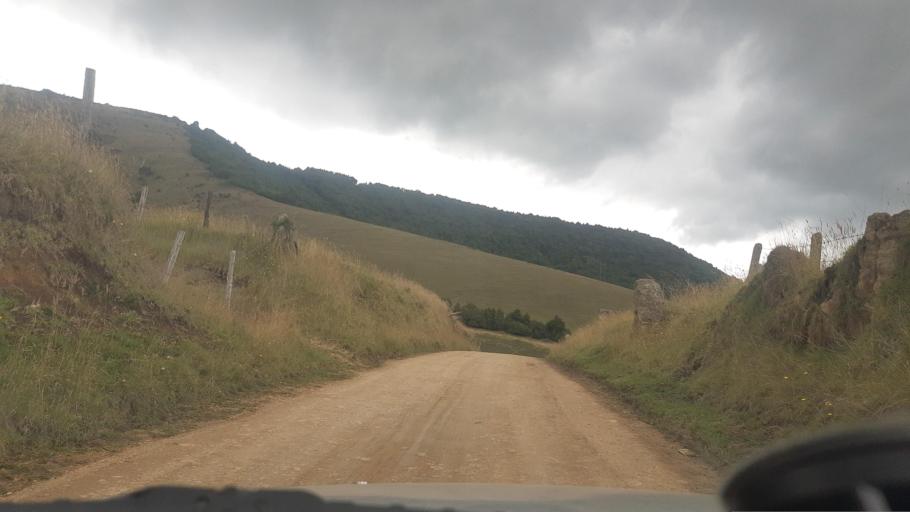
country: CO
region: Cundinamarca
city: Suesca
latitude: 5.1553
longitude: -73.8006
